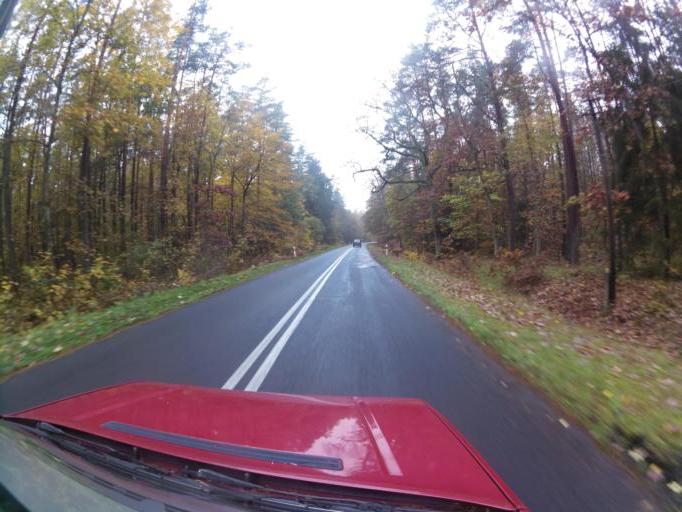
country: PL
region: West Pomeranian Voivodeship
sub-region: Powiat policki
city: Dobra
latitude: 53.5855
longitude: 14.3793
